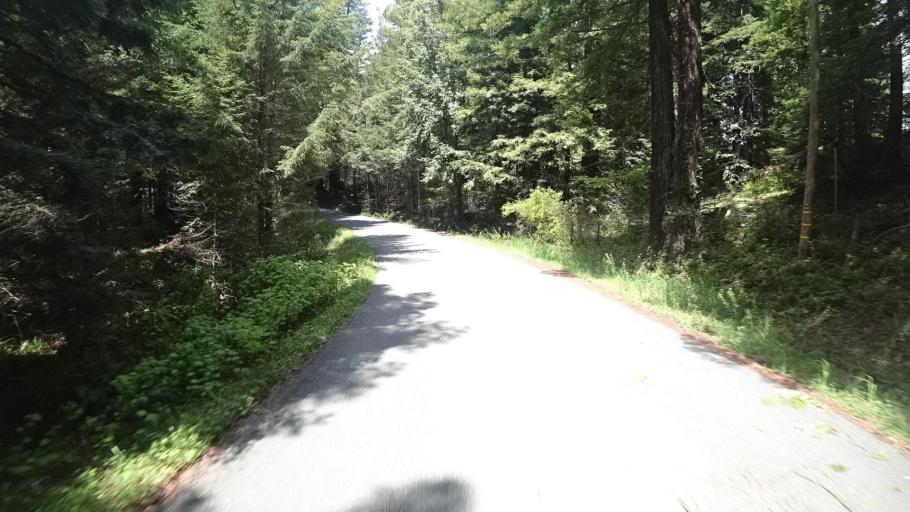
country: US
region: California
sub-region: Humboldt County
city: Blue Lake
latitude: 40.8440
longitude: -123.9210
